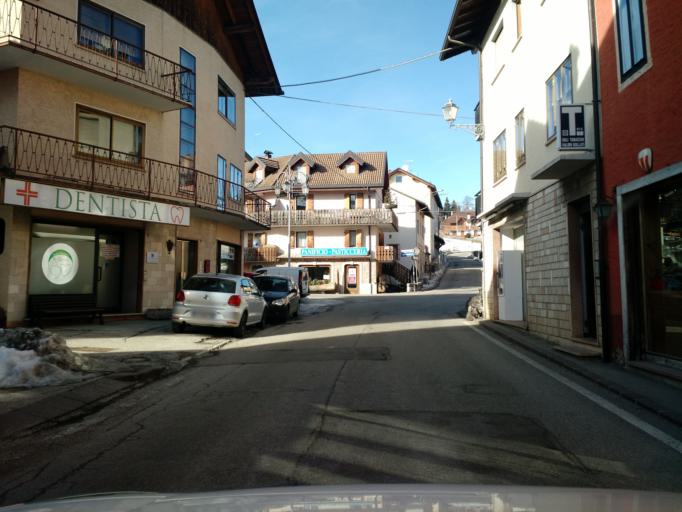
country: IT
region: Veneto
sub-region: Provincia di Vicenza
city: Roana
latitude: 45.8757
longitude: 11.4625
